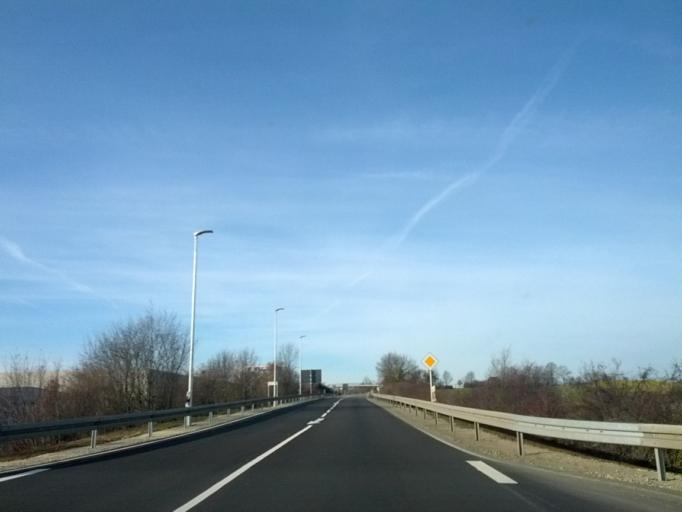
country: DE
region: Baden-Wuerttemberg
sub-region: Regierungsbezirk Stuttgart
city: Ellwangen
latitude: 48.9584
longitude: 10.1742
